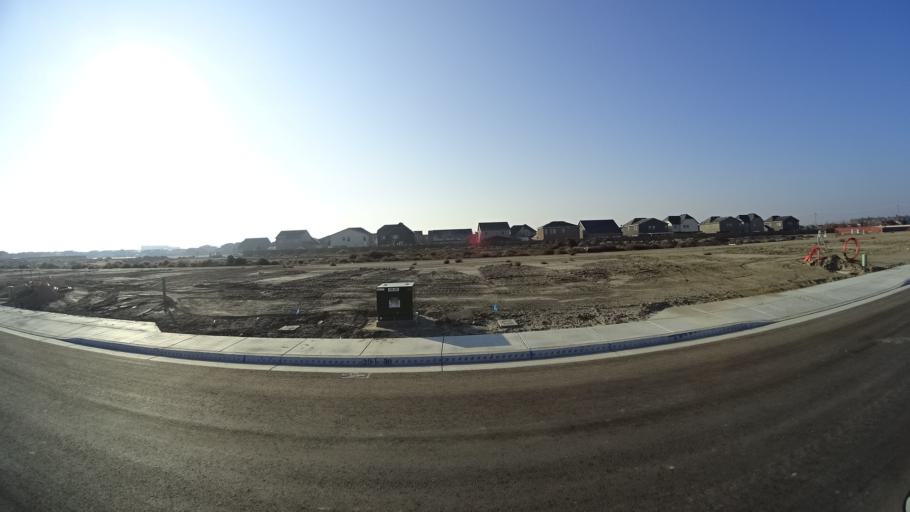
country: US
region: California
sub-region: Kern County
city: Greenacres
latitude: 35.2937
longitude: -119.1160
